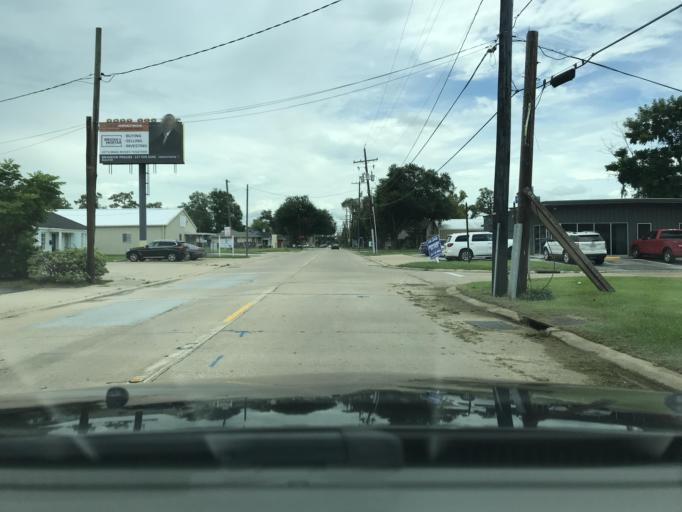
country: US
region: Louisiana
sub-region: Calcasieu Parish
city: Lake Charles
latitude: 30.2033
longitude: -93.2169
